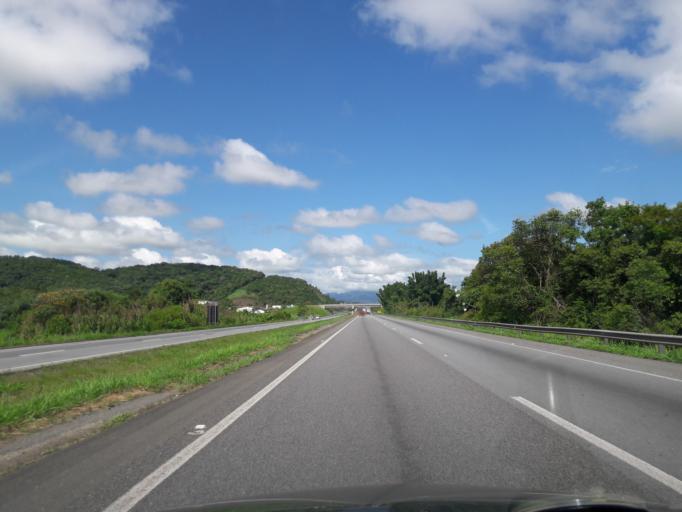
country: BR
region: Sao Paulo
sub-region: Jacupiranga
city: Jacupiranga
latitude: -24.6834
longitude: -47.9862
